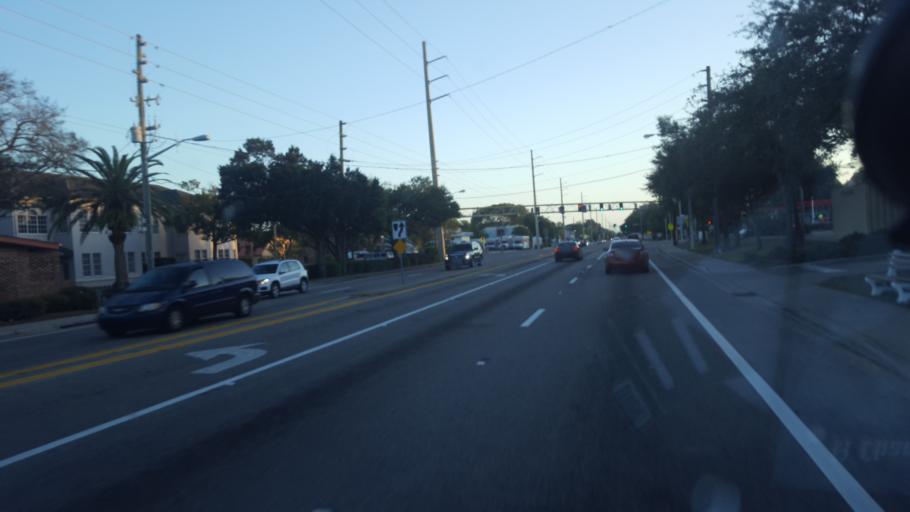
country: US
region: Florida
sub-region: Sarasota County
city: Sarasota
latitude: 27.3386
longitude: -82.5141
